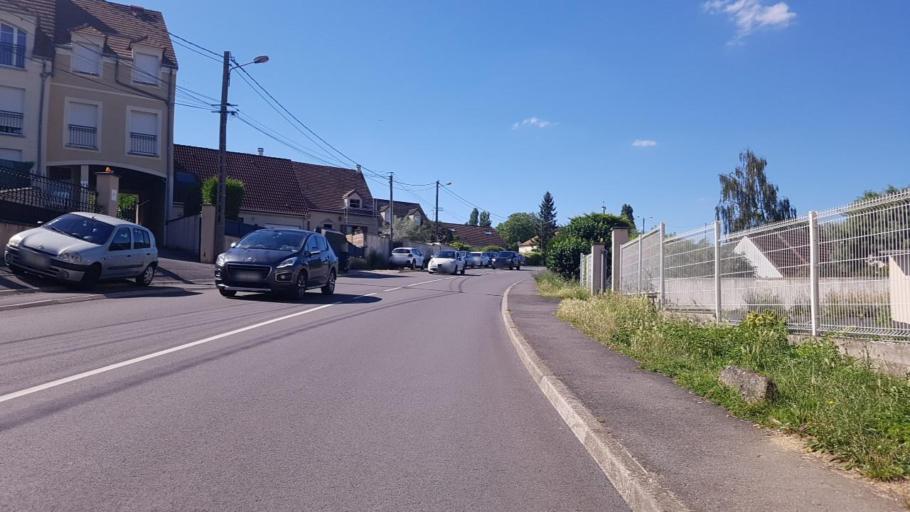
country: FR
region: Ile-de-France
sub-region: Departement de Seine-et-Marne
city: Villenoy
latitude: 48.9490
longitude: 2.8656
